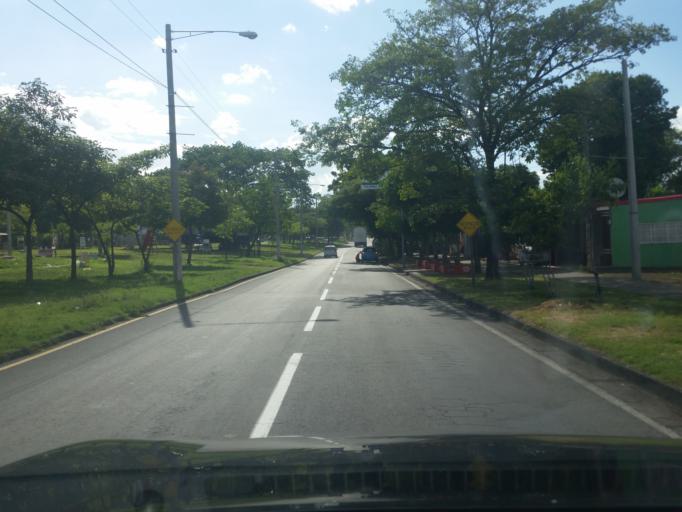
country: NI
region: Managua
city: Managua
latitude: 12.1555
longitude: -86.2832
